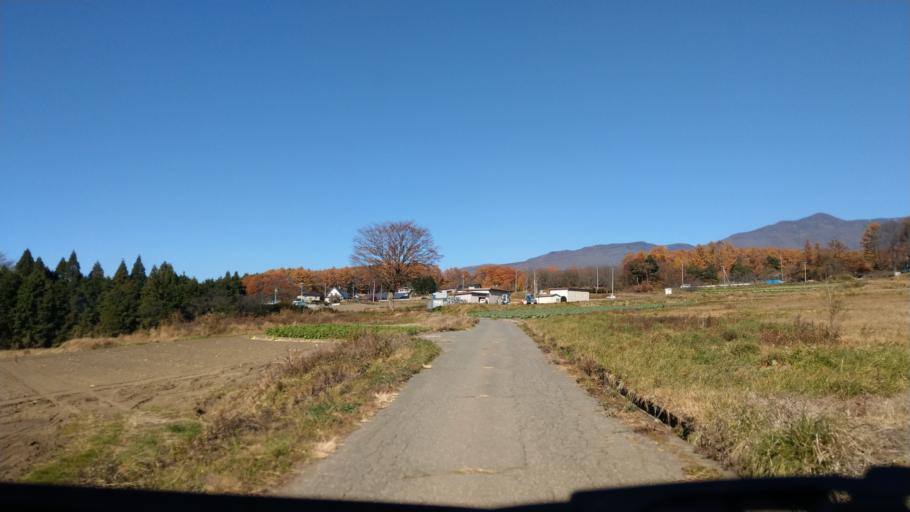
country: JP
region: Nagano
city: Komoro
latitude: 36.3366
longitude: 138.4581
